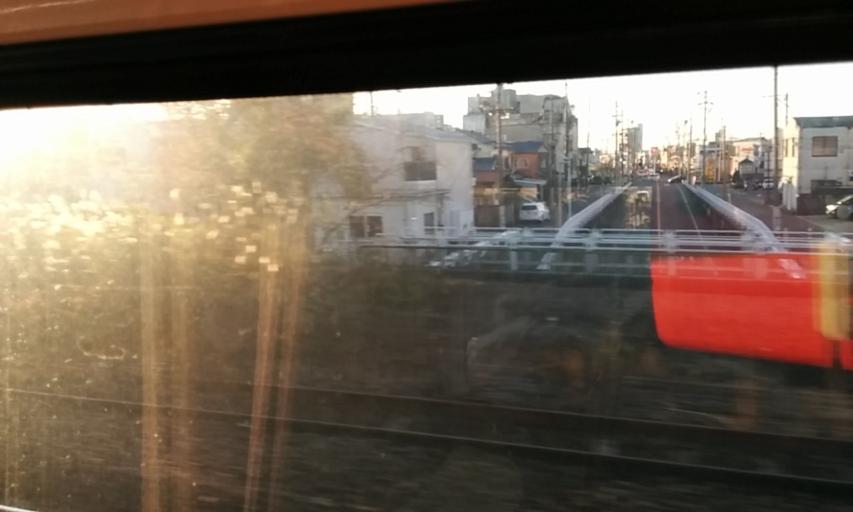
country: JP
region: Aichi
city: Kasugai
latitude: 35.2109
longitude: 136.9530
